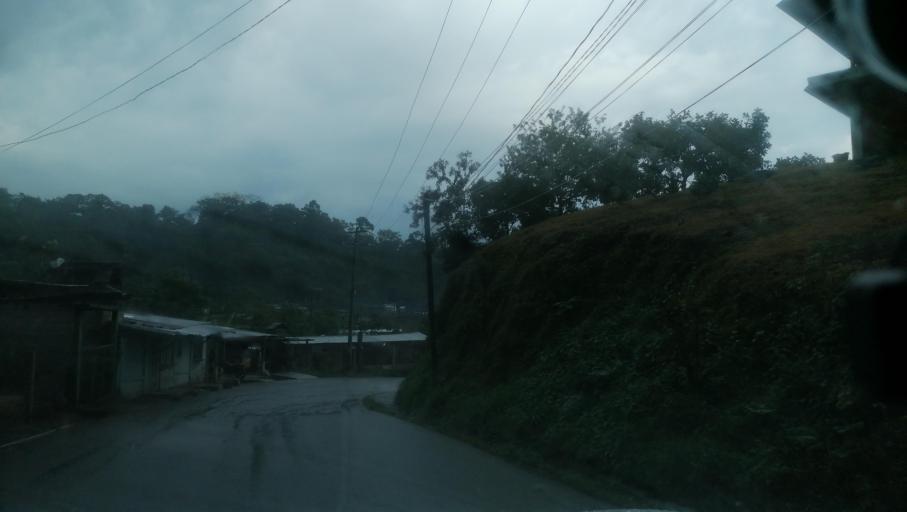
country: MX
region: Chiapas
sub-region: Cacahoatan
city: Benito Juarez
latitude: 15.0564
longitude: -92.1929
